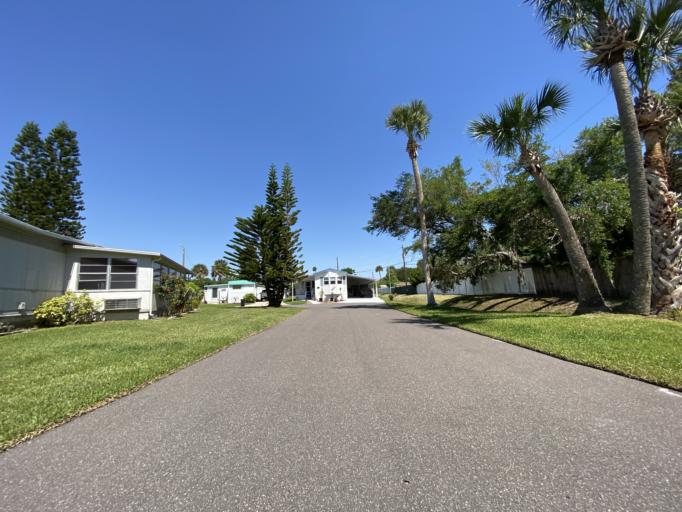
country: US
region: Florida
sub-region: Volusia County
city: South Daytona
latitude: 29.1596
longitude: -81.0173
